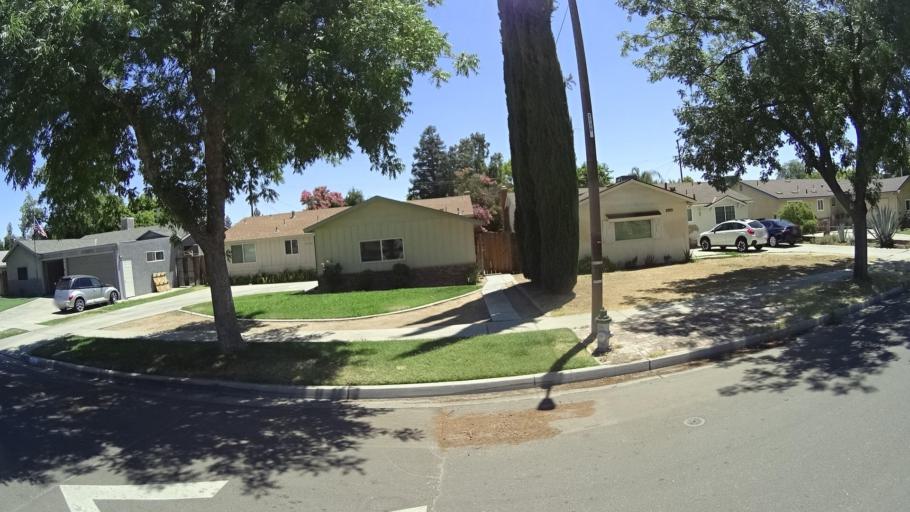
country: US
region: California
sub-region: Fresno County
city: Fresno
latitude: 36.8037
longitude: -119.7792
